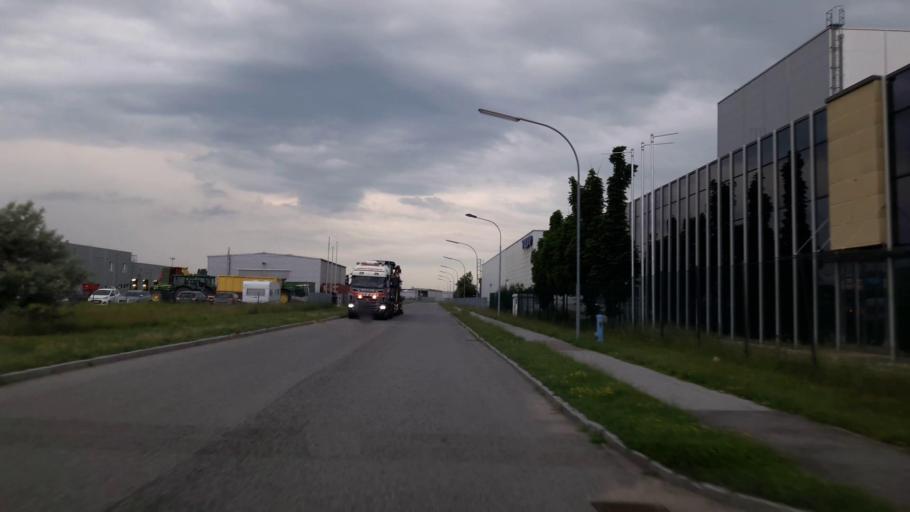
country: AT
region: Burgenland
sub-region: Politischer Bezirk Neusiedl am See
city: Bruckneudorf
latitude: 48.0339
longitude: 16.8020
